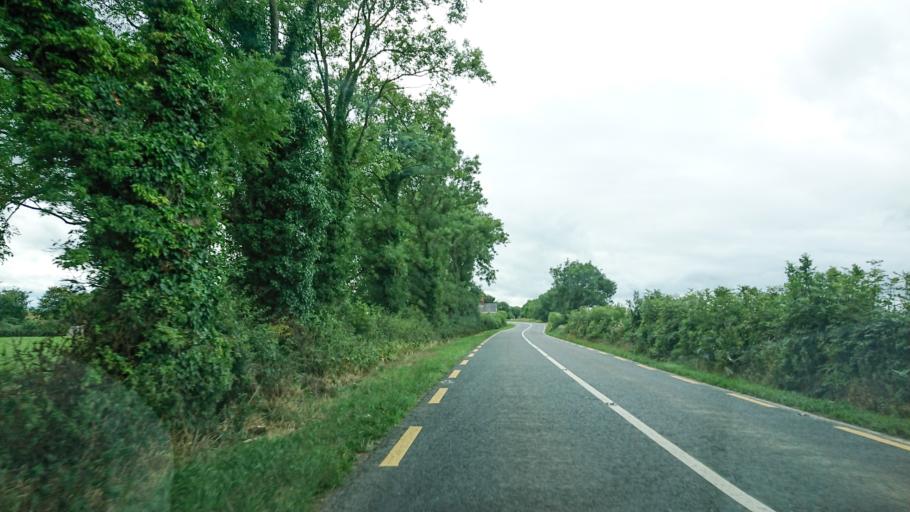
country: IE
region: Munster
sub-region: County Cork
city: Mallow
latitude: 52.1535
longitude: -8.5847
